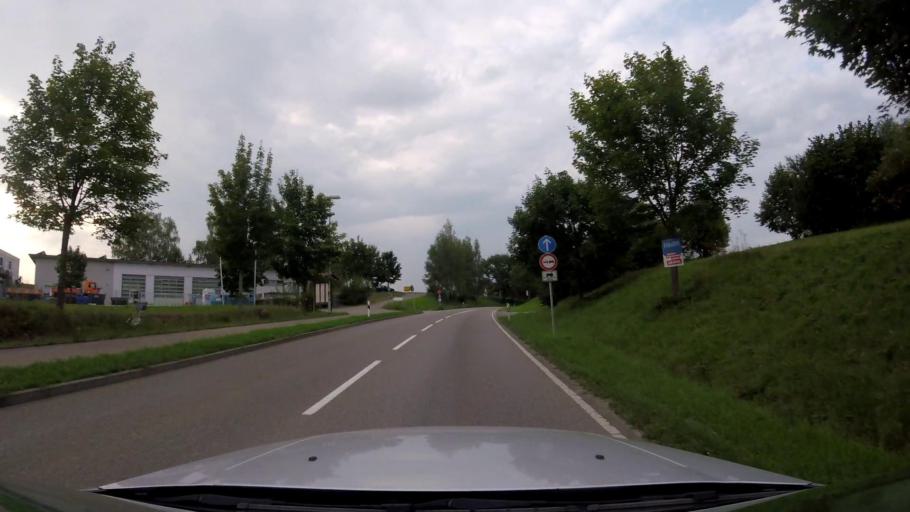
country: DE
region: Baden-Wuerttemberg
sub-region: Regierungsbezirk Stuttgart
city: Allmersbach im Tal
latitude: 48.9118
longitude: 9.4653
